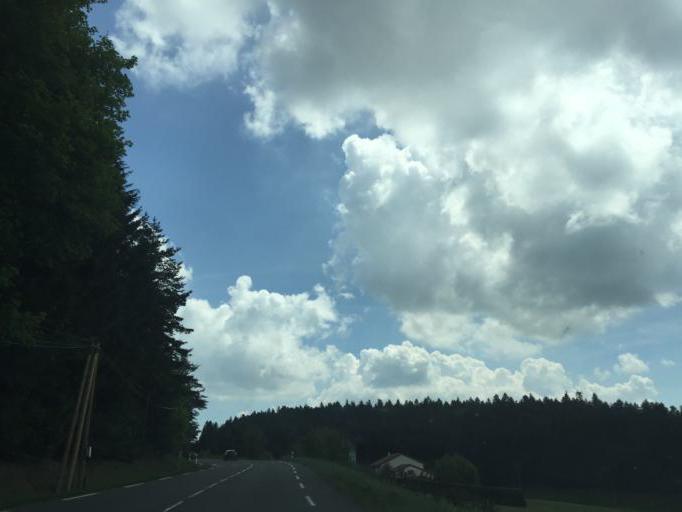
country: FR
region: Rhone-Alpes
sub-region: Departement de la Loire
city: Saint-Genest-Malifaux
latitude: 45.3726
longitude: 4.4468
